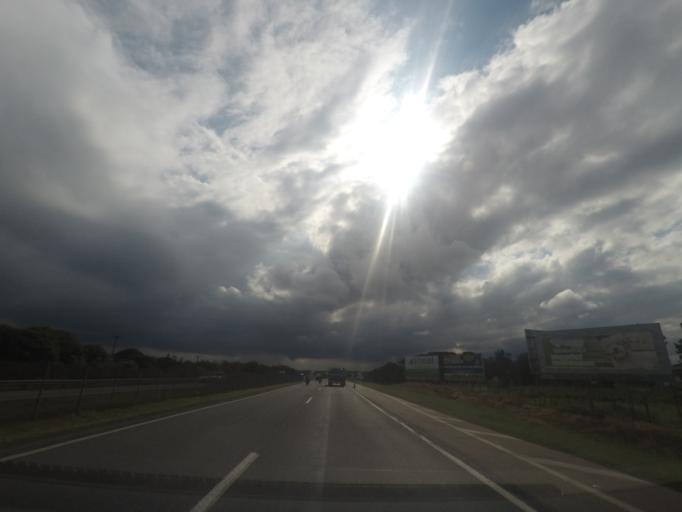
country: BR
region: Parana
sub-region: Sao Jose Dos Pinhais
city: Sao Jose dos Pinhais
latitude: -25.5009
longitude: -49.1516
